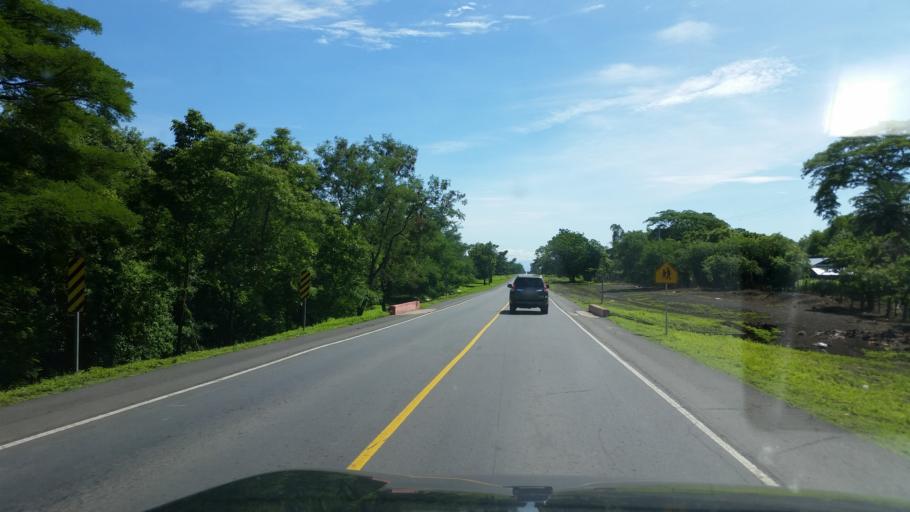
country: NI
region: Chinandega
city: El Viejo
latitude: 12.7469
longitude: -87.0700
